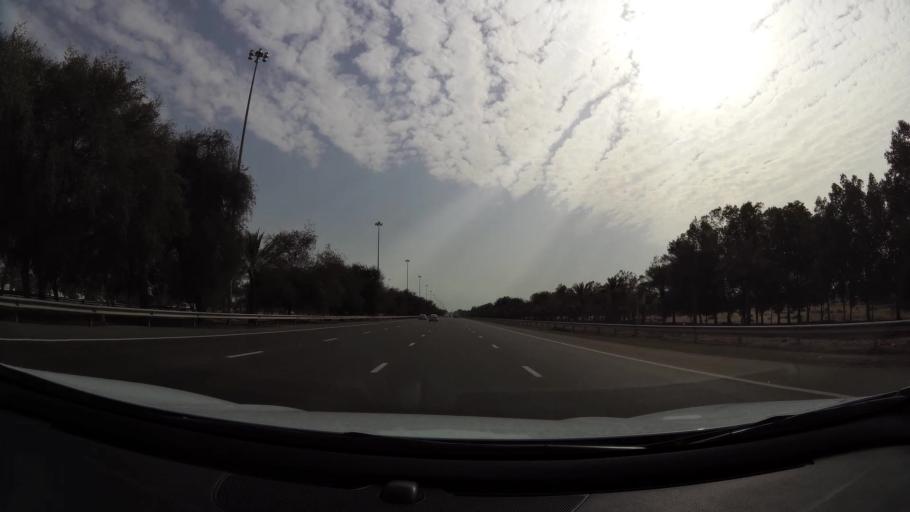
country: AE
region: Abu Dhabi
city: Abu Dhabi
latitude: 24.5146
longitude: 54.6876
